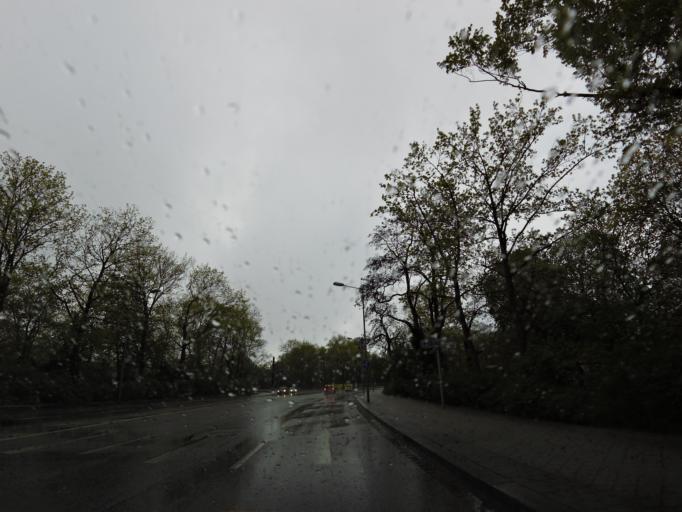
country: DE
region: Saxony-Anhalt
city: Magdeburg
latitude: 52.1152
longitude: 11.6305
